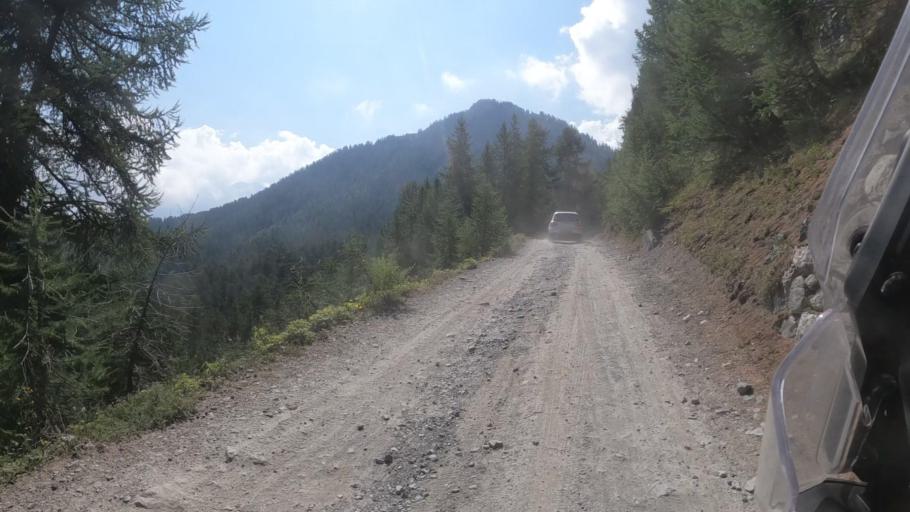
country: IT
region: Piedmont
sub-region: Provincia di Torino
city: Cesana Torinese
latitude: 44.9118
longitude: 6.7997
